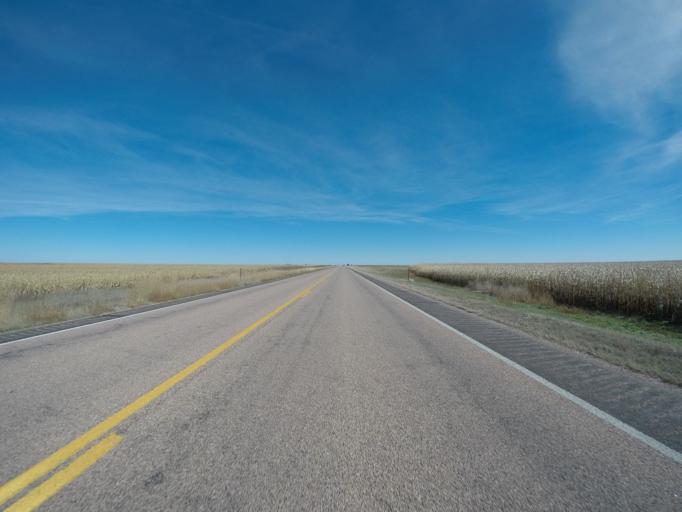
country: US
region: Colorado
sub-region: Kit Carson County
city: Burlington
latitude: 39.6564
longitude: -102.5884
